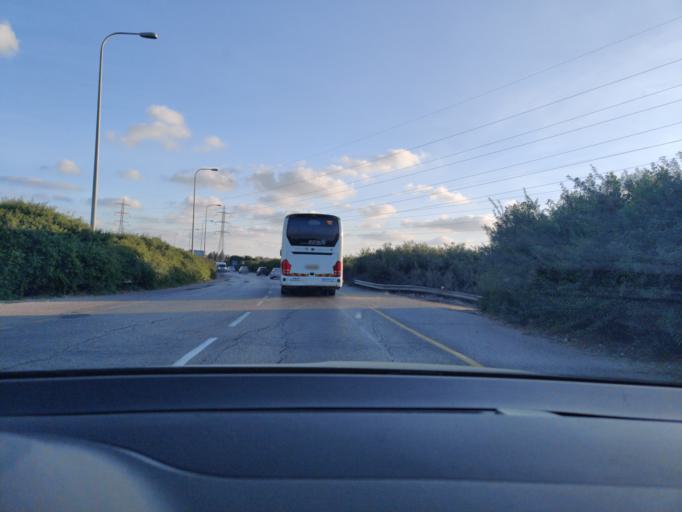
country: IL
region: Haifa
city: Hadera
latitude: 32.4464
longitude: 34.9404
